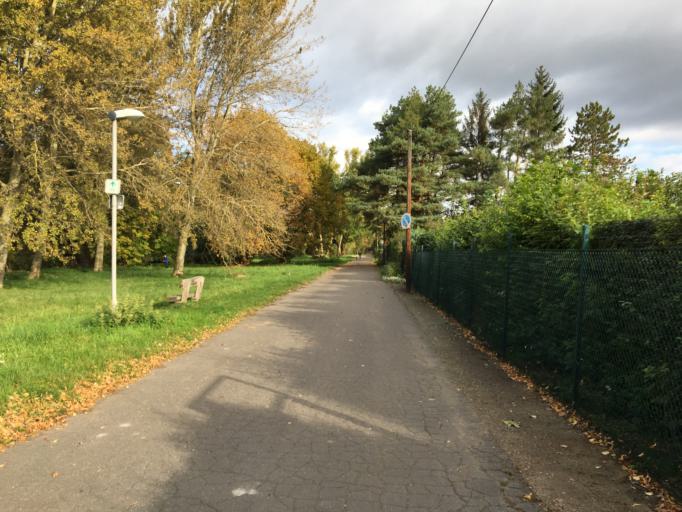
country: DE
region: Lower Saxony
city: Braunschweig
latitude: 52.2821
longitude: 10.5131
